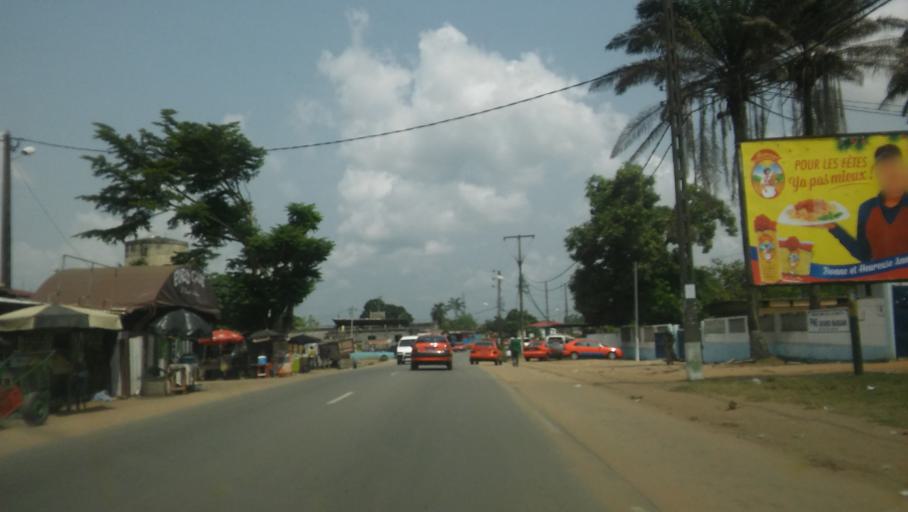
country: CI
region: Sud-Comoe
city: Grand-Bassam
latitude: 5.2141
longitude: -3.7316
